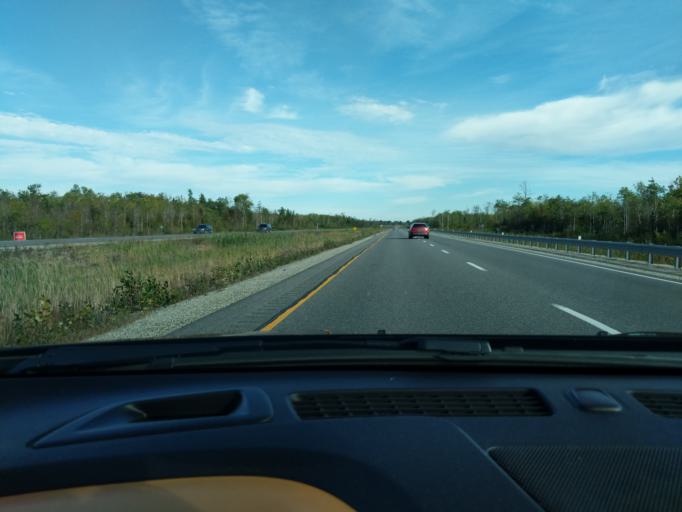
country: CA
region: Ontario
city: Collingwood
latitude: 44.4653
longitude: -80.1251
